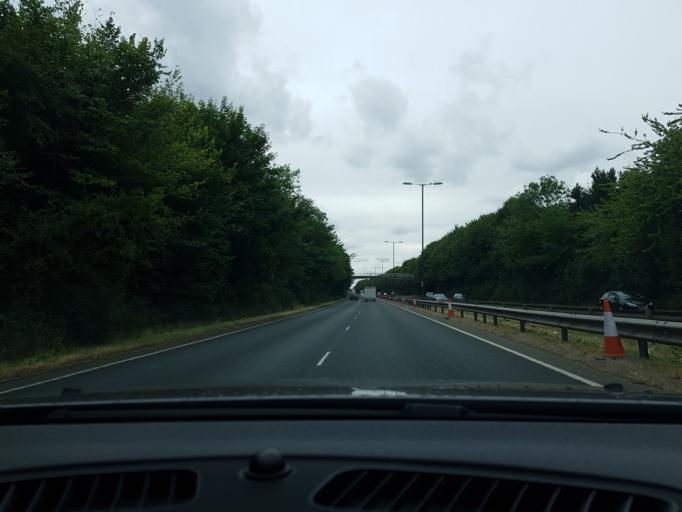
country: GB
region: England
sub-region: Hampshire
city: Basingstoke
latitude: 51.2791
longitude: -1.0864
